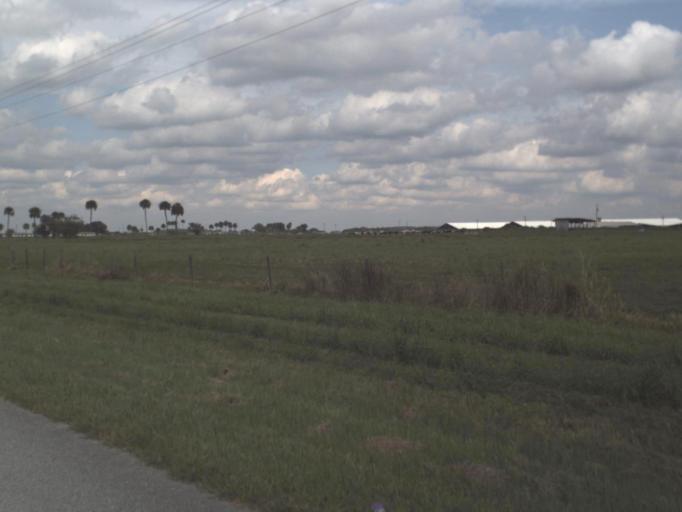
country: US
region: Florida
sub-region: Okeechobee County
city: Cypress Quarters
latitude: 27.4088
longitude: -80.8142
